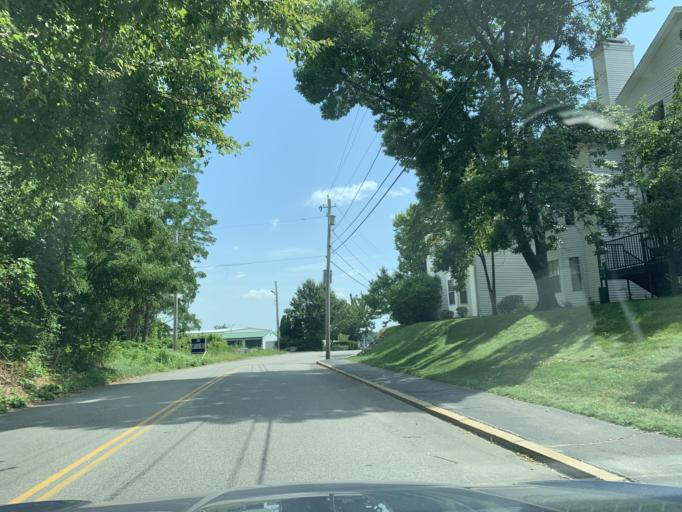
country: US
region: Rhode Island
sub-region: Providence County
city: Cranston
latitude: 41.7882
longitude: -71.4760
